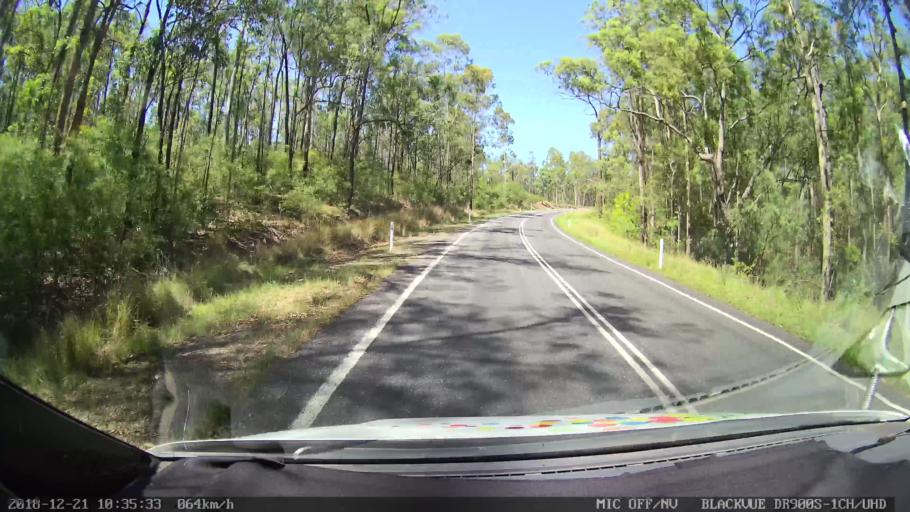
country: AU
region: New South Wales
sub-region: Clarence Valley
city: South Grafton
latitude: -29.6203
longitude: 152.6434
